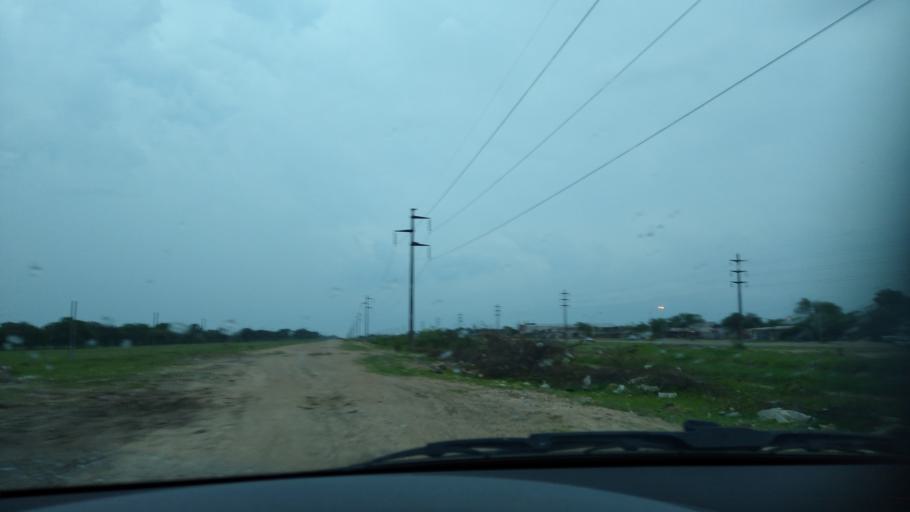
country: AR
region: Chaco
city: Puerto Vilelas
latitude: -27.5028
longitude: -58.9726
